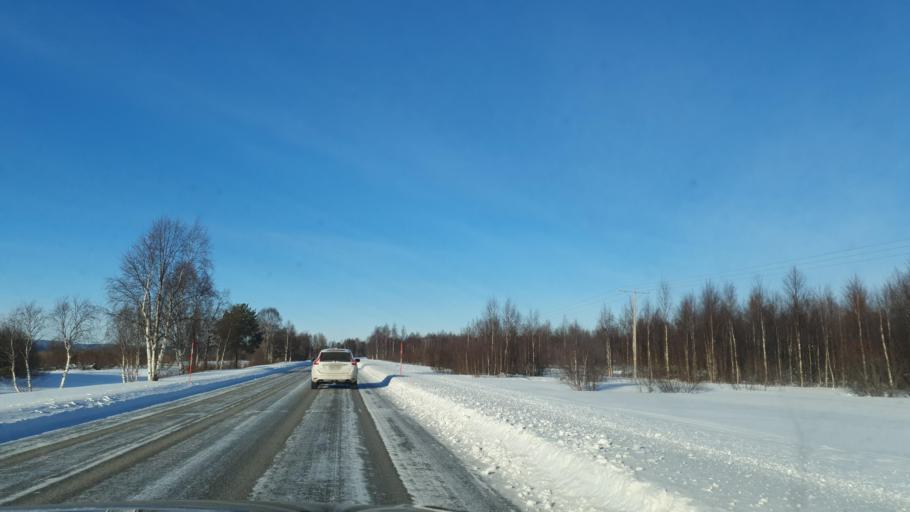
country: SE
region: Norrbotten
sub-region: Overtornea Kommun
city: OEvertornea
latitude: 66.3980
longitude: 23.6819
